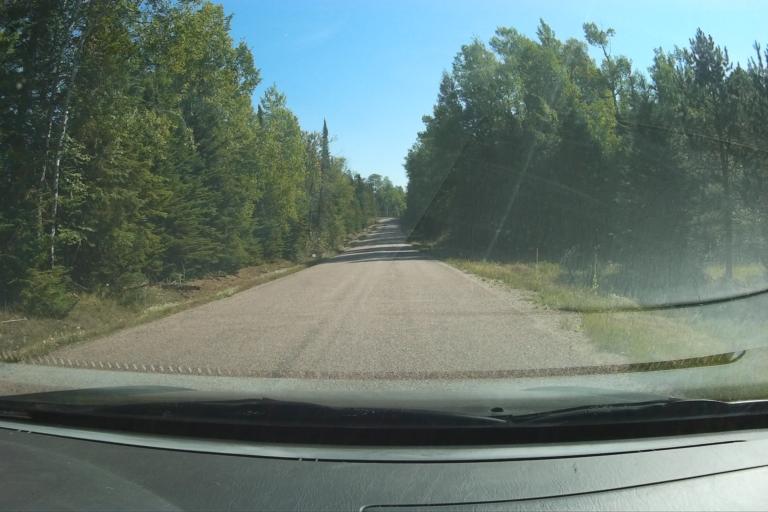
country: CA
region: Ontario
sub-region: Thunder Bay District
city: Thunder Bay
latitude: 48.3478
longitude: -88.8032
